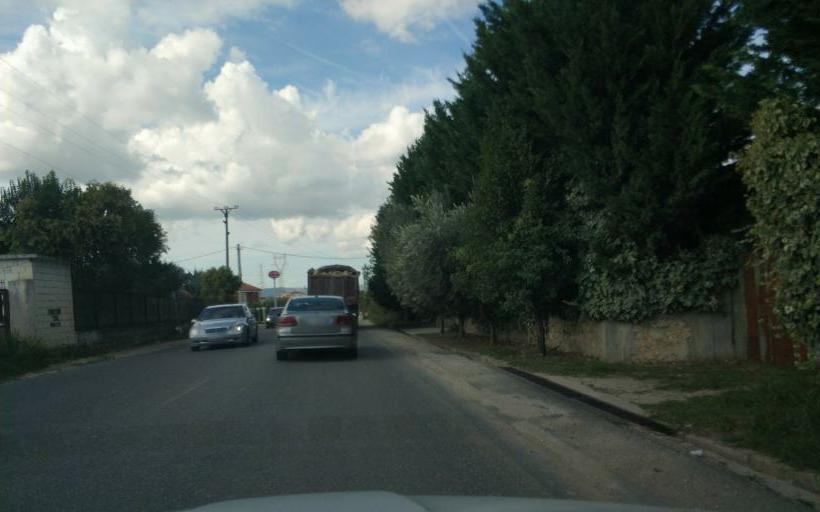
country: AL
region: Durres
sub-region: Rrethi i Krujes
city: Fushe-Kruje
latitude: 41.4762
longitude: 19.7474
